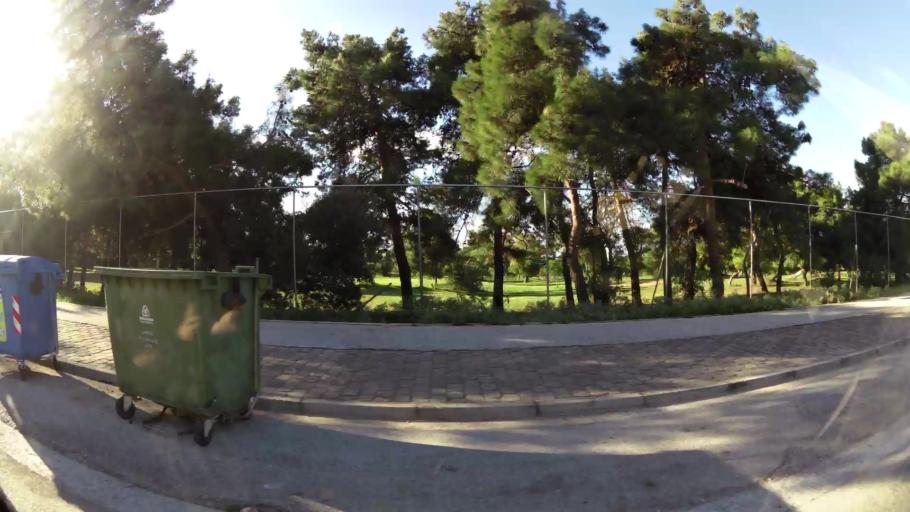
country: GR
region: Attica
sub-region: Nomarchia Athinas
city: Glyfada
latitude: 37.8744
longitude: 23.7494
